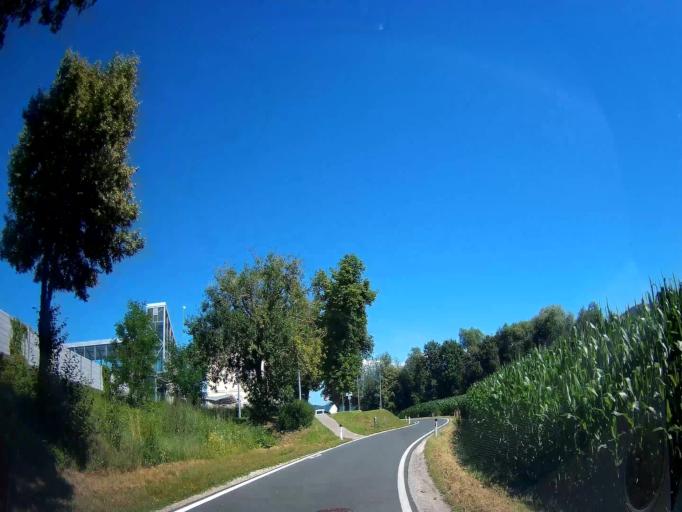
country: AT
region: Carinthia
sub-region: Politischer Bezirk Klagenfurt Land
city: Grafenstein
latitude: 46.6189
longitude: 14.4585
